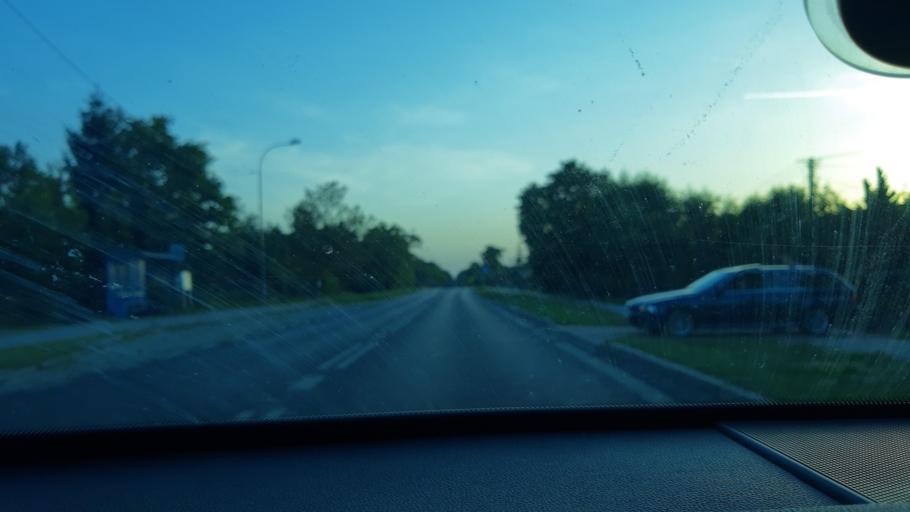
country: PL
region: Lodz Voivodeship
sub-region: Powiat zdunskowolski
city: Zapolice
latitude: 51.6050
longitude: 18.8472
